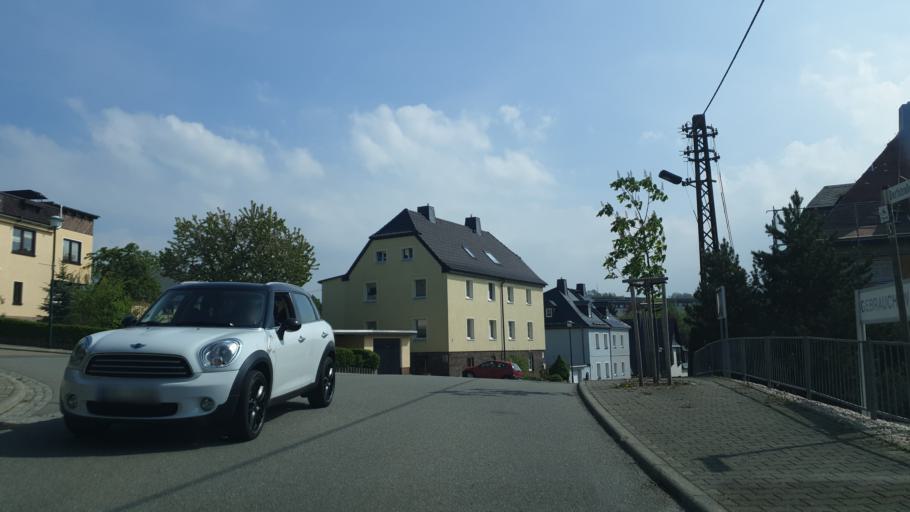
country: DE
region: Saxony
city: Stollberg
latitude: 50.7196
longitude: 12.7895
